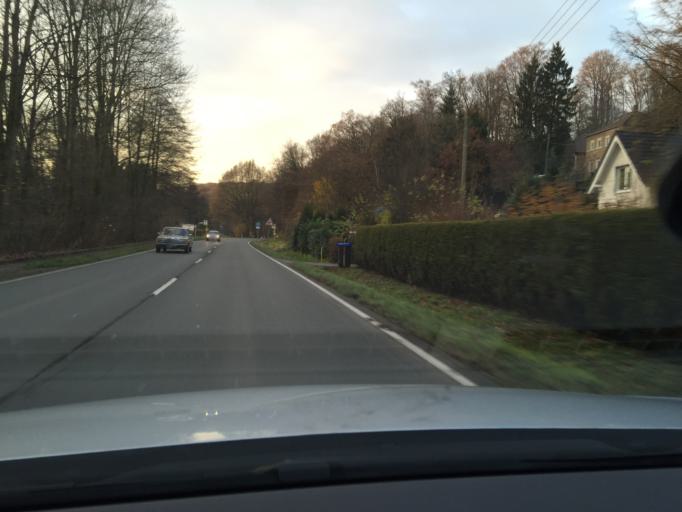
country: DE
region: North Rhine-Westphalia
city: Hattingen
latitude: 51.3700
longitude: 7.1836
